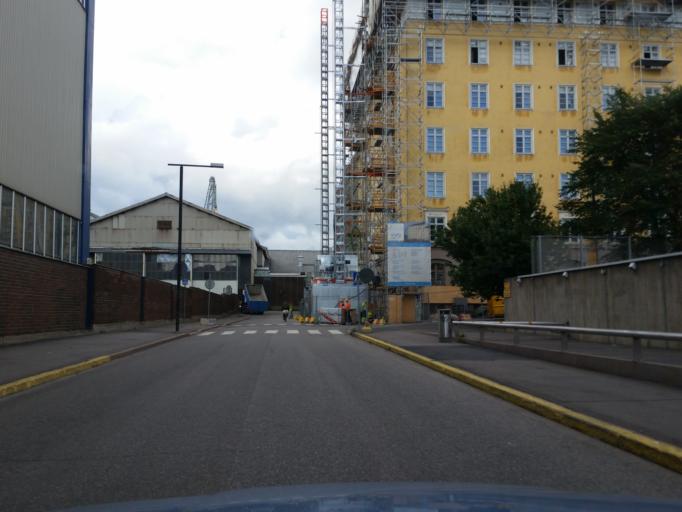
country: FI
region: Uusimaa
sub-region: Helsinki
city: Helsinki
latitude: 60.1559
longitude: 24.9304
